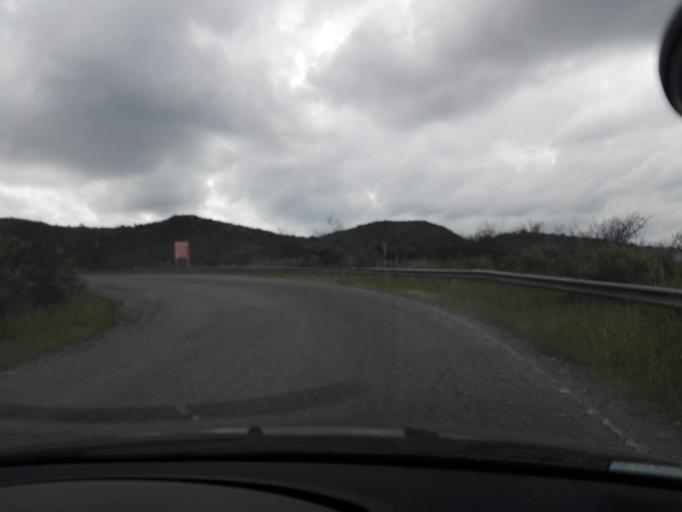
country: AR
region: Cordoba
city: Alta Gracia
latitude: -31.5899
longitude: -64.5075
